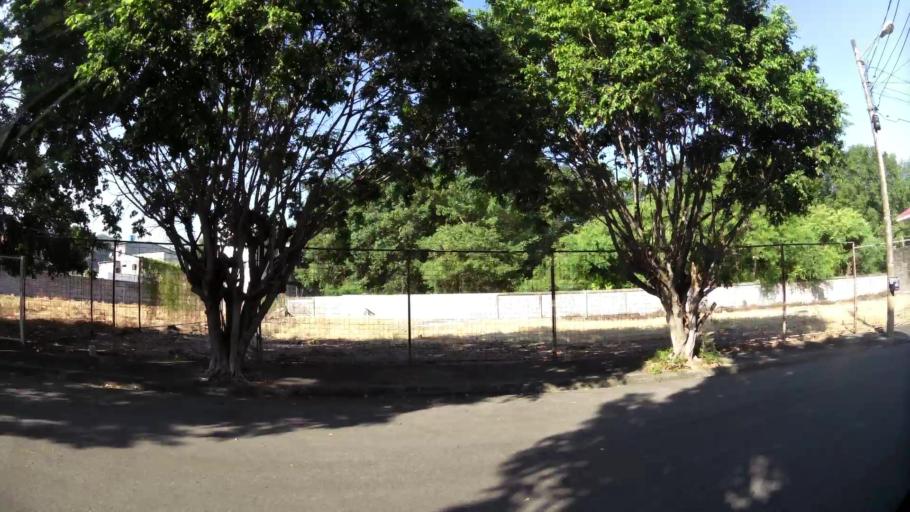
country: EC
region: Guayas
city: Santa Lucia
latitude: -2.1941
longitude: -79.9622
